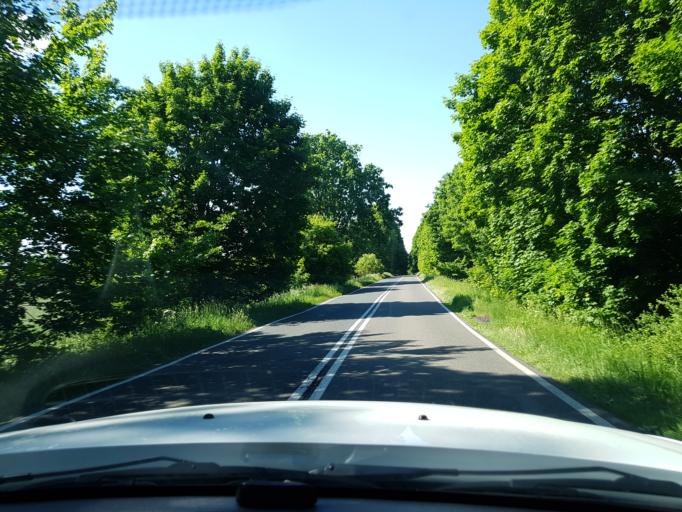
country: PL
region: West Pomeranian Voivodeship
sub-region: Powiat gryfinski
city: Gryfino
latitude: 53.1842
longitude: 14.5378
